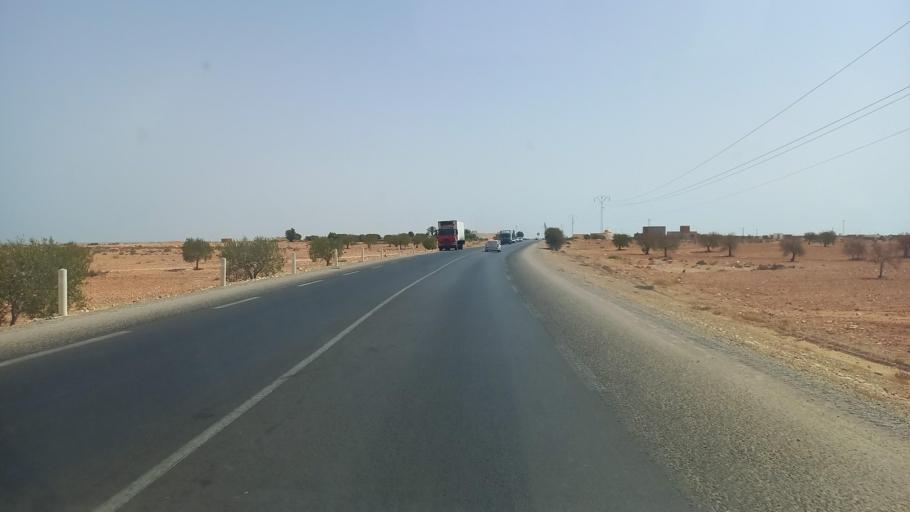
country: TN
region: Madanin
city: Medenine
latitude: 33.3886
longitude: 10.7084
